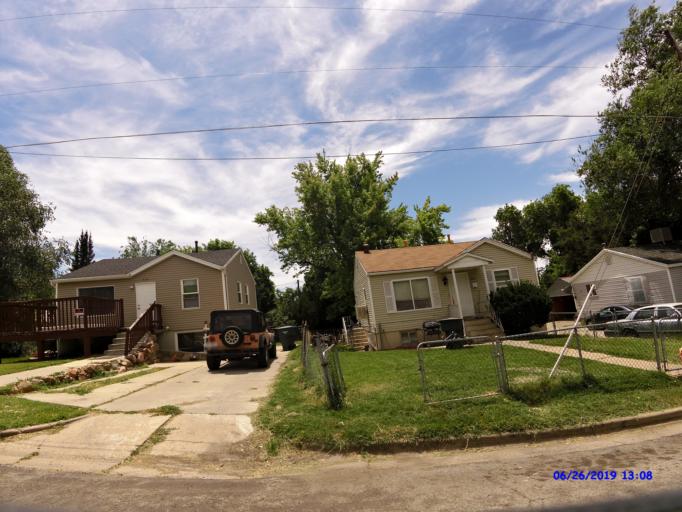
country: US
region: Utah
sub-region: Weber County
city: Ogden
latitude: 41.2122
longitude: -111.9643
